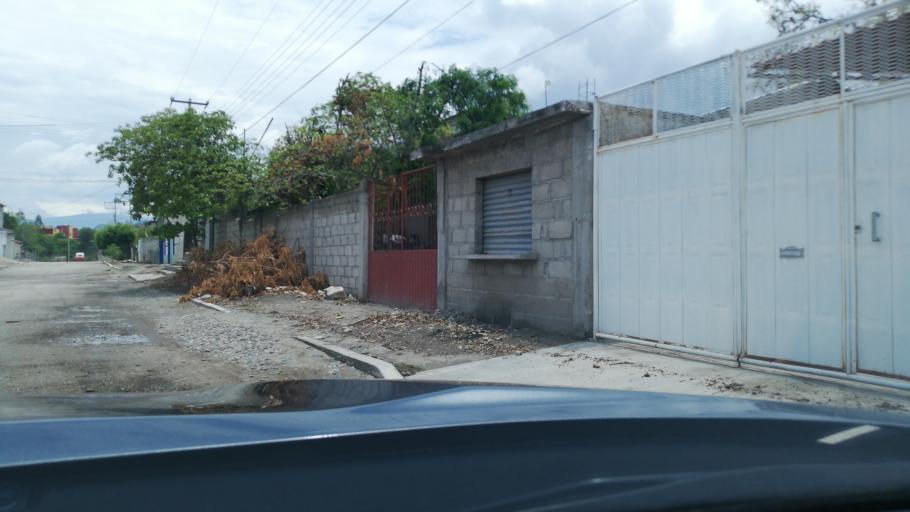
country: MX
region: Oaxaca
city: Santa Maria Jalapa del Marques
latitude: 16.4465
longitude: -95.4424
